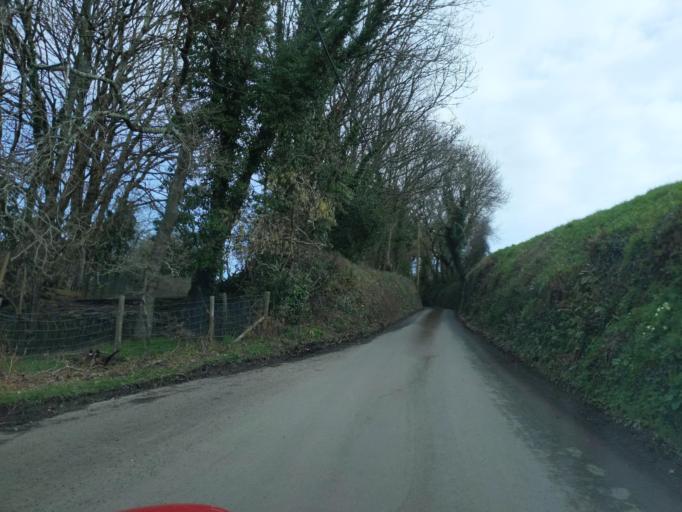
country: GB
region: England
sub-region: Devon
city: Yealmpton
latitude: 50.3639
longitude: -4.0107
